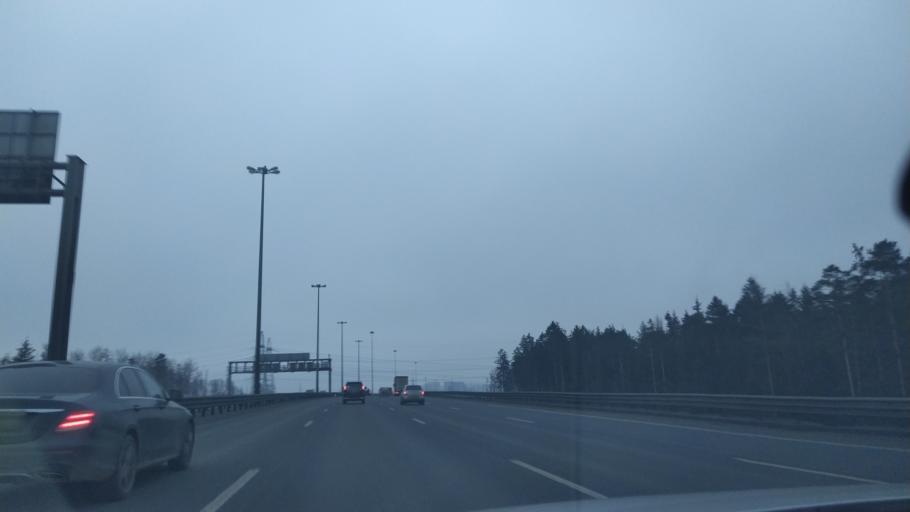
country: RU
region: St.-Petersburg
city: Krasnogvargeisky
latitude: 59.9344
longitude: 30.5379
